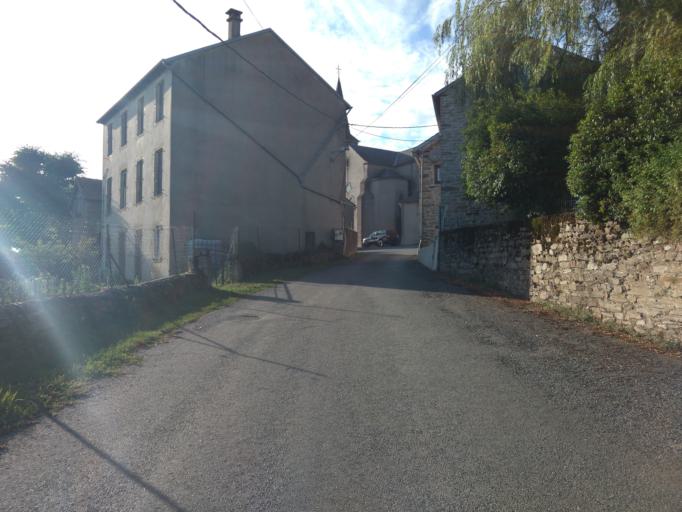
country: FR
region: Midi-Pyrenees
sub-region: Departement de l'Aveyron
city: Requista
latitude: 44.0736
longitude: 2.5307
